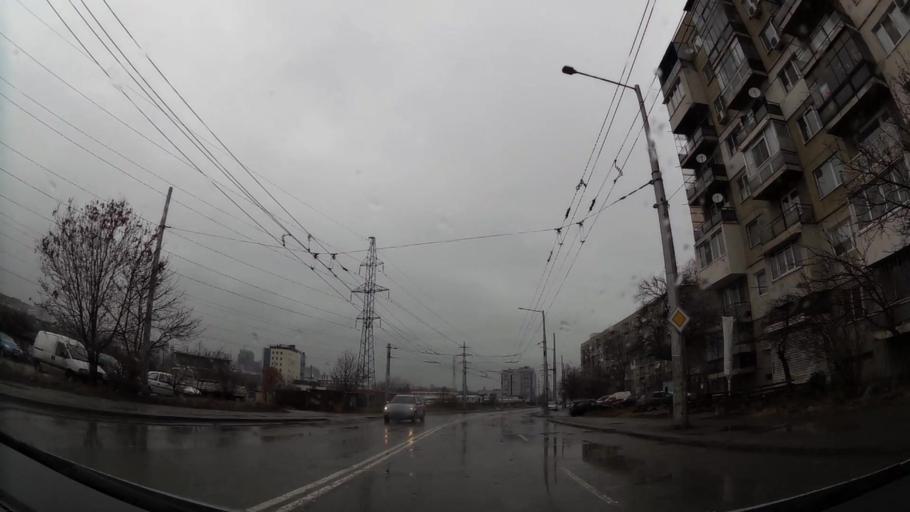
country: BG
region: Sofia-Capital
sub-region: Stolichna Obshtina
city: Sofia
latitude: 42.6585
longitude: 23.3966
